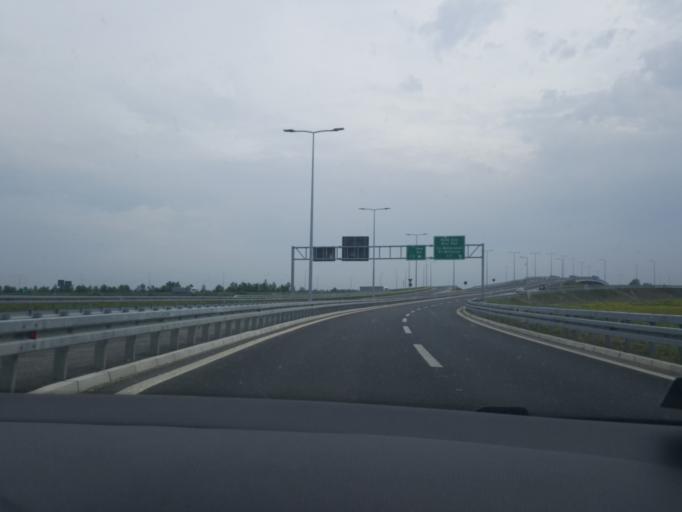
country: RS
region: Central Serbia
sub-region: Belgrade
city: Surcin
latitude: 44.7714
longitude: 20.2799
